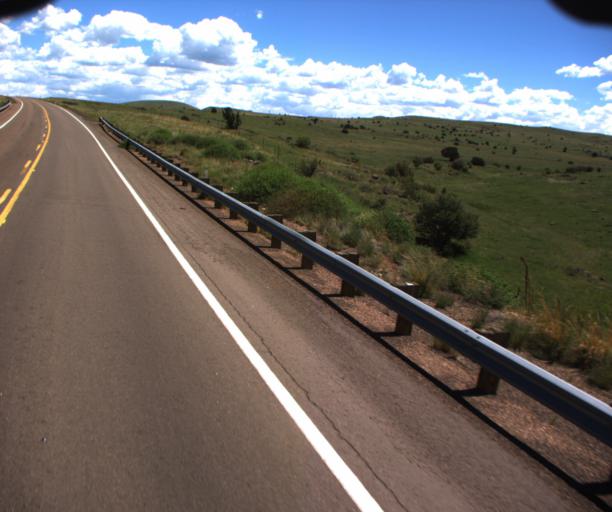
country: US
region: Arizona
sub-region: Apache County
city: Springerville
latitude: 34.2232
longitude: -109.4852
